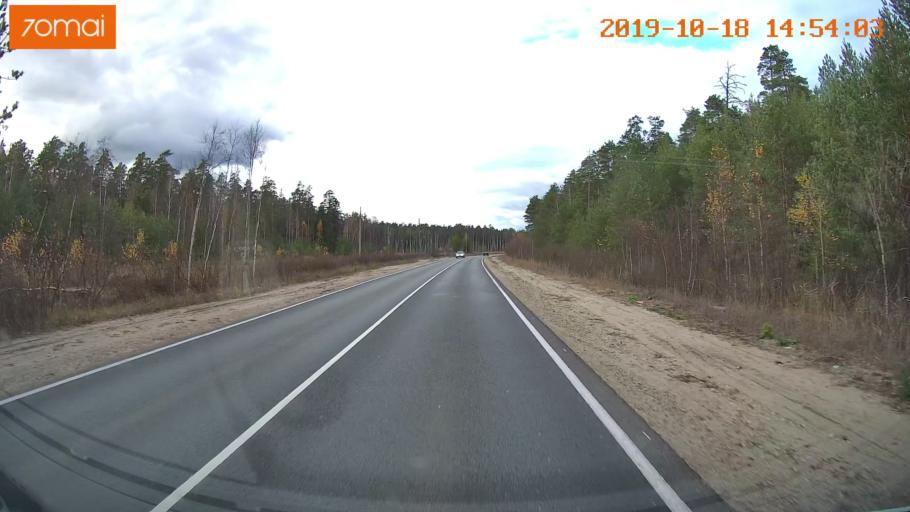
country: RU
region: Vladimir
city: Kurlovo
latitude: 55.4360
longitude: 40.6053
